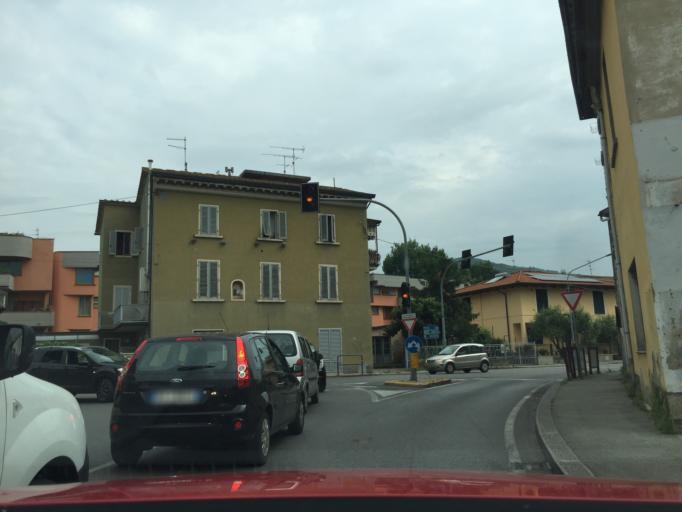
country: IT
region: Tuscany
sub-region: Provincia di Pistoia
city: Pieve a Nievole
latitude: 43.8826
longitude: 10.8084
